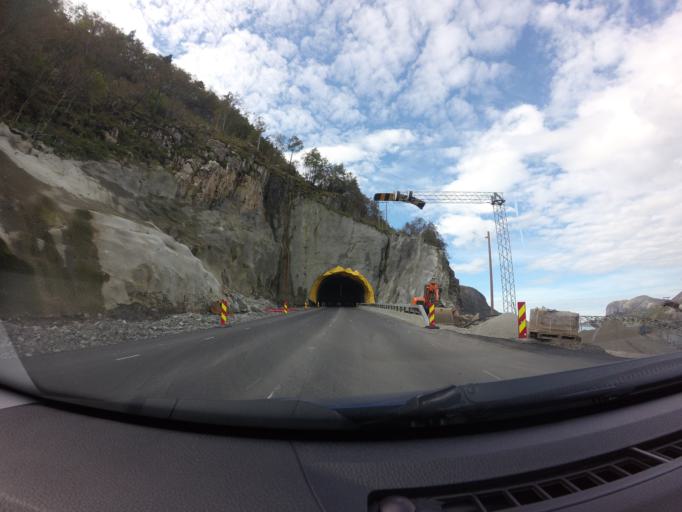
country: NO
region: Rogaland
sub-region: Forsand
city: Forsand
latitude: 58.8370
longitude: 6.1687
